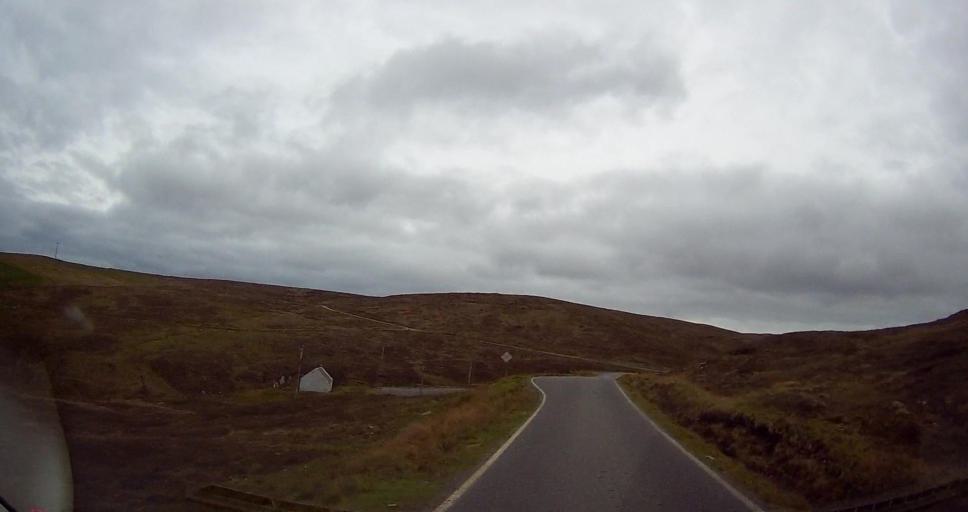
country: GB
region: Scotland
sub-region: Shetland Islands
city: Shetland
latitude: 60.5516
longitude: -1.0592
